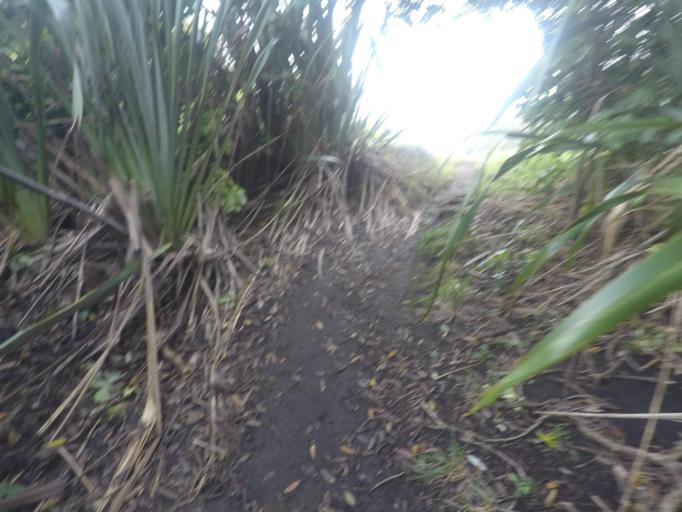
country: NZ
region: Auckland
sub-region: Auckland
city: Muriwai Beach
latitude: -36.8813
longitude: 174.4389
